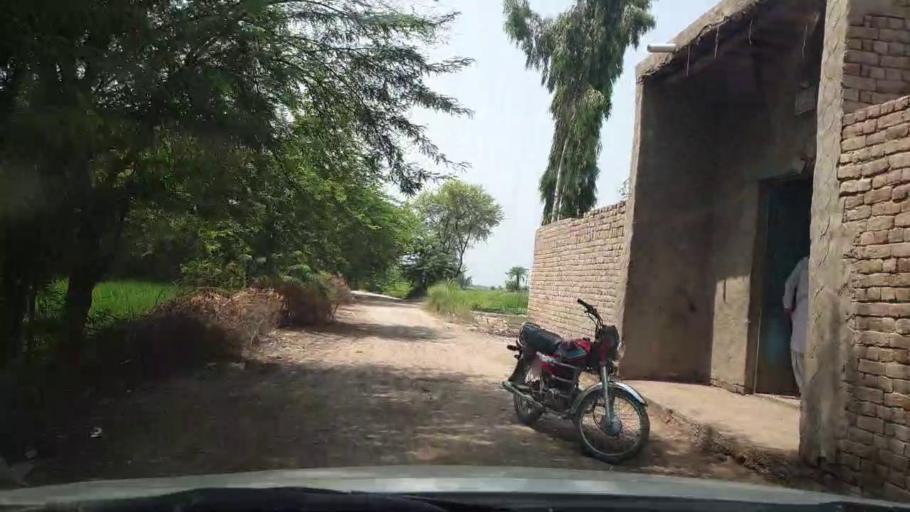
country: PK
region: Sindh
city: Rustam jo Goth
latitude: 27.9772
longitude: 68.7219
